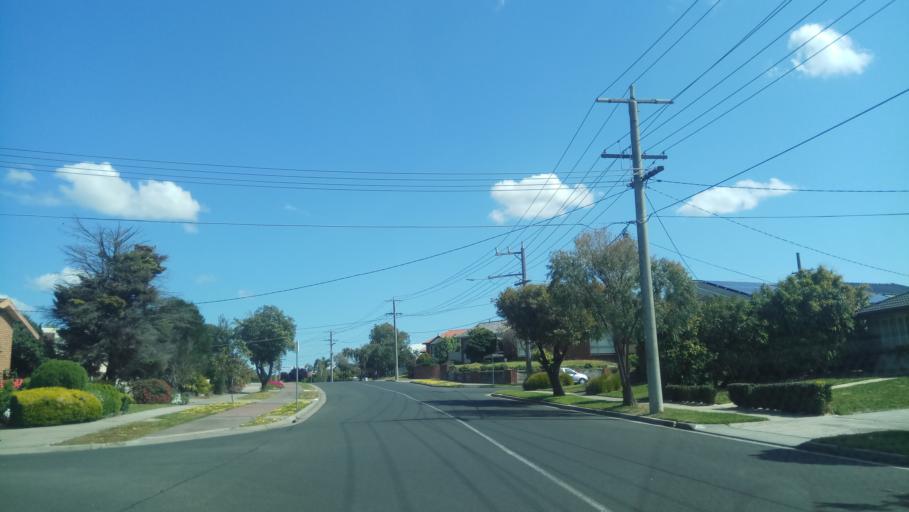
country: AU
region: Victoria
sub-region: Kingston
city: Dingley Village
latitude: -37.9749
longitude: 145.1180
